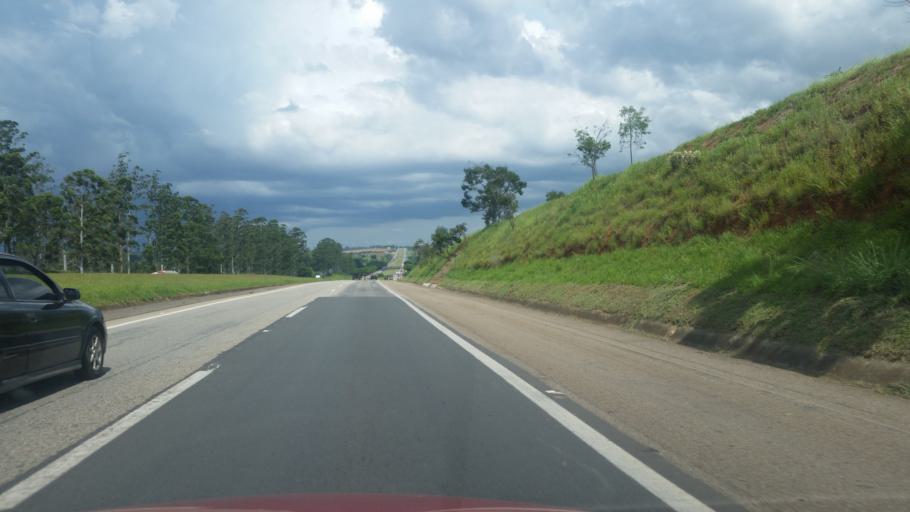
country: BR
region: Sao Paulo
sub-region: Tatui
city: Tatui
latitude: -23.2842
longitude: -47.7809
